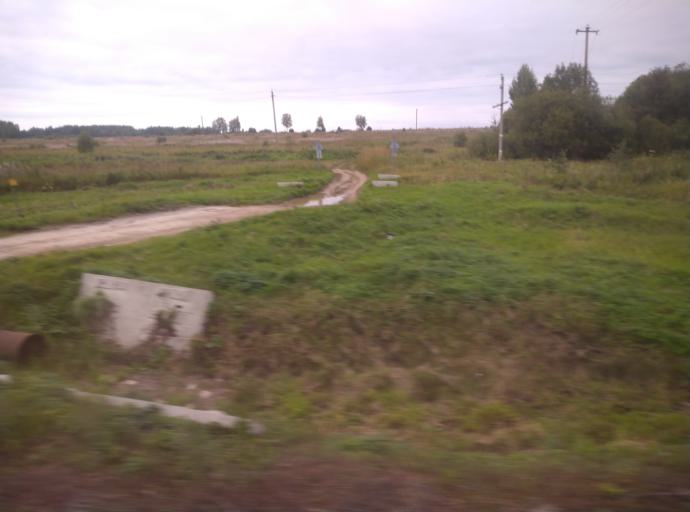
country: RU
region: Kostroma
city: Nerekhta
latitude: 57.4543
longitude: 40.4515
